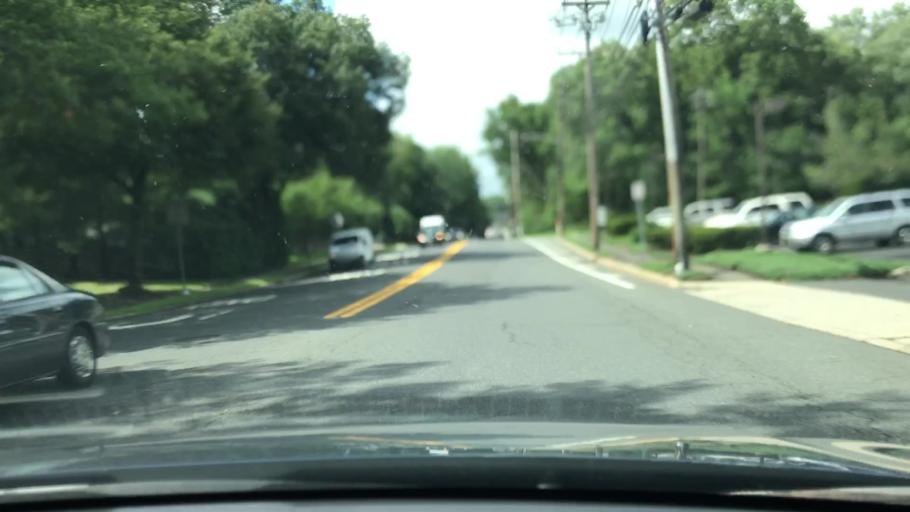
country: US
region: New Jersey
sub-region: Bergen County
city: Wyckoff
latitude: 41.0197
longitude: -74.1671
